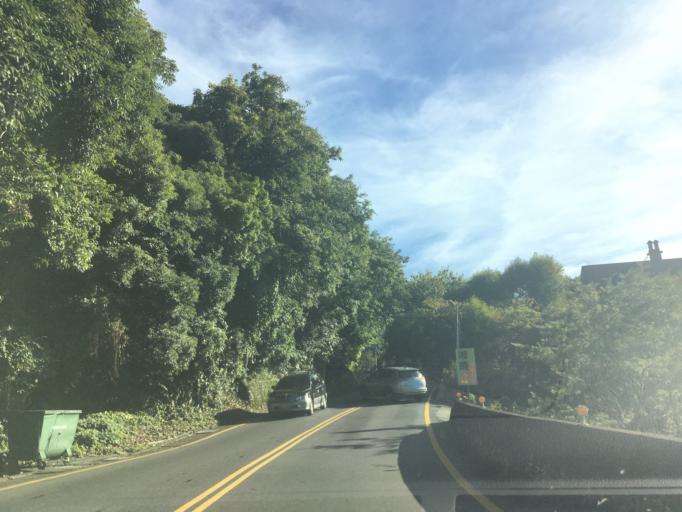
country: TW
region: Taiwan
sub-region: Nantou
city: Puli
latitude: 24.0429
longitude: 121.1578
